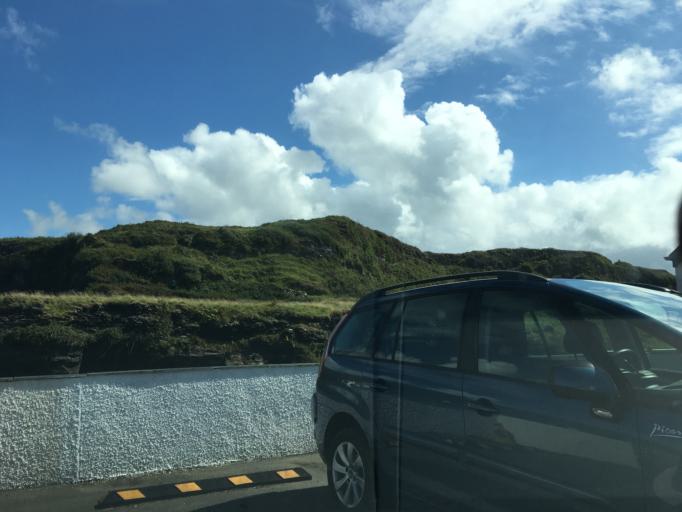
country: GB
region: Scotland
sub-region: Argyll and Bute
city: Isle Of Mull
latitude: 56.2555
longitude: -5.6525
